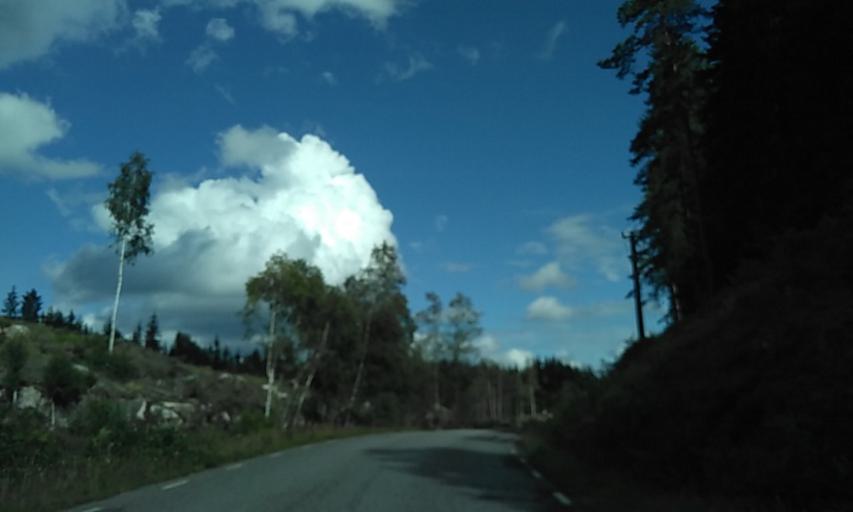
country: SE
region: Vaestra Goetaland
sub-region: Vargarda Kommun
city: Jonstorp
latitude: 57.9371
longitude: 12.7419
